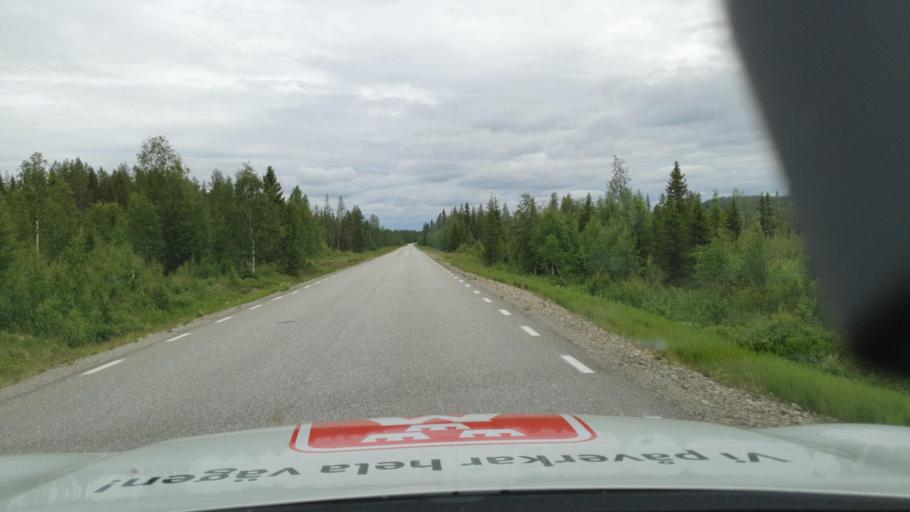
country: SE
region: Vaesterbotten
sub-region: Lycksele Kommun
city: Soderfors
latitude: 64.3290
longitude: 18.1463
